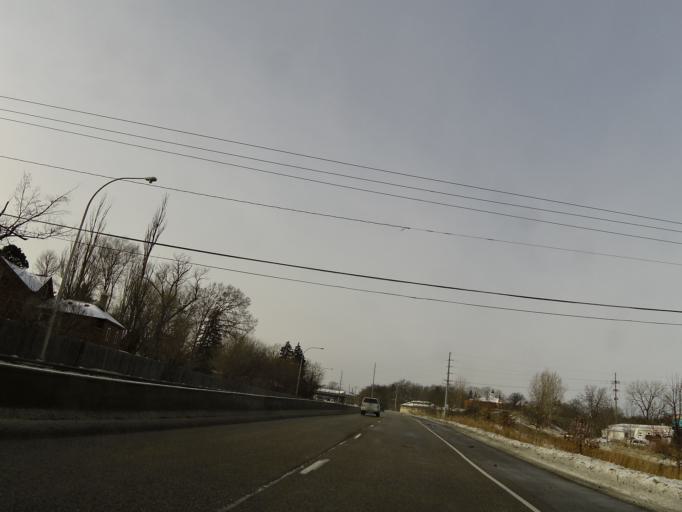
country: US
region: Minnesota
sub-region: Hennepin County
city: Excelsior
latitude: 44.9011
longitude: -93.5576
